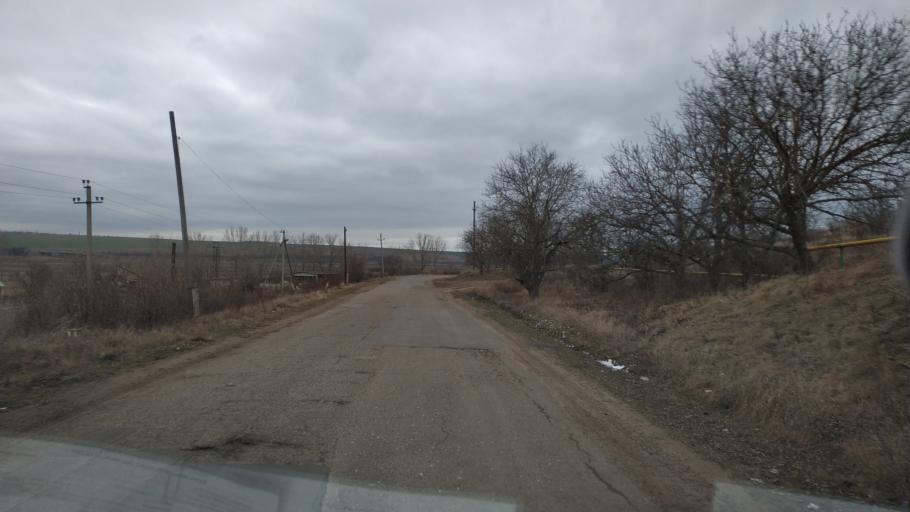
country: MD
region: Causeni
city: Causeni
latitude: 46.6663
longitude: 29.4561
